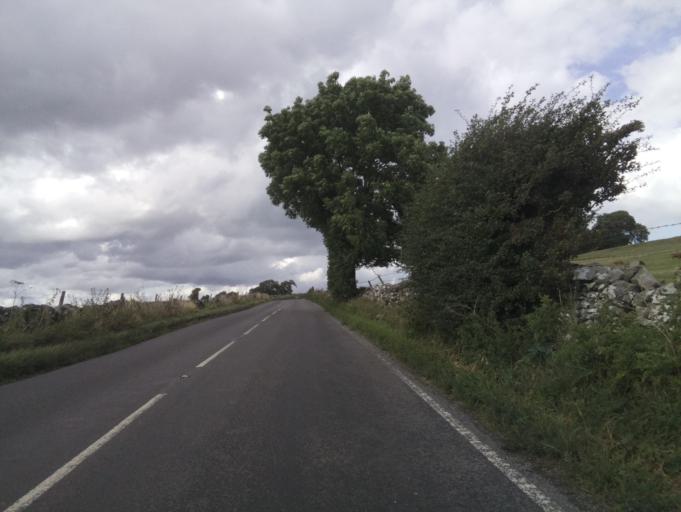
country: GB
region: England
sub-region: North Yorkshire
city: Leyburn
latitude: 54.3652
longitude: -1.8235
